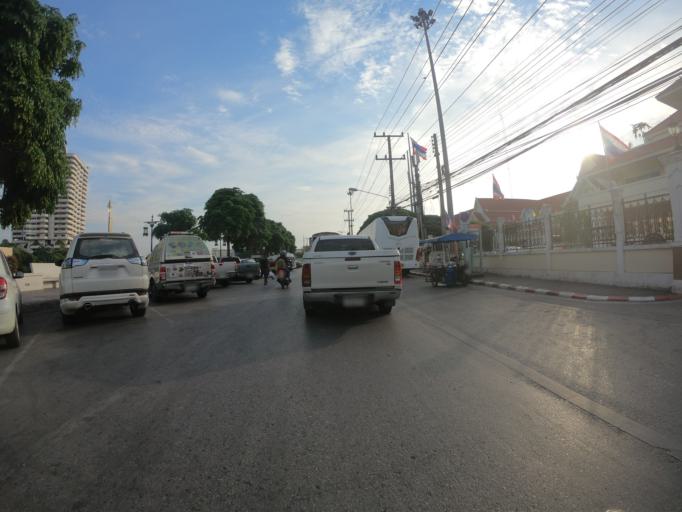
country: TH
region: Chiang Mai
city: Chiang Mai
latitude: 18.7958
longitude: 98.9992
